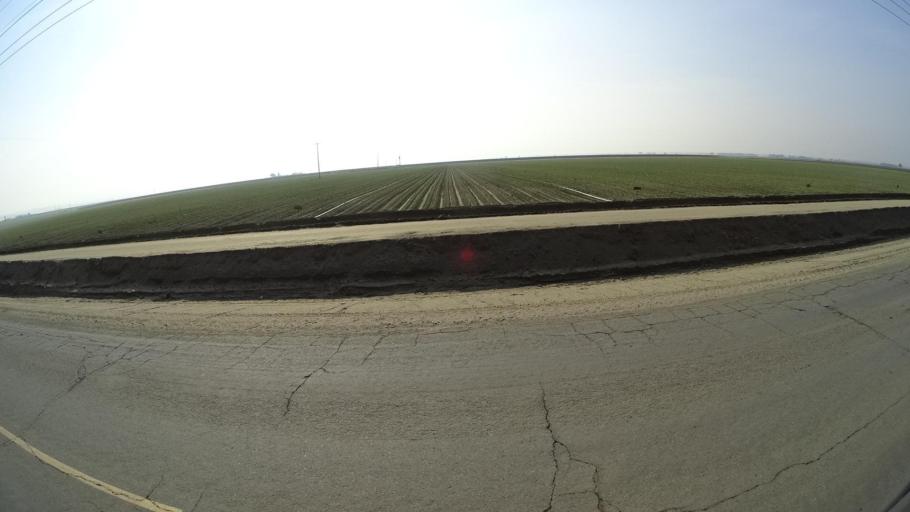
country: US
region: California
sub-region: Kern County
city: Arvin
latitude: 35.0928
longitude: -118.8519
